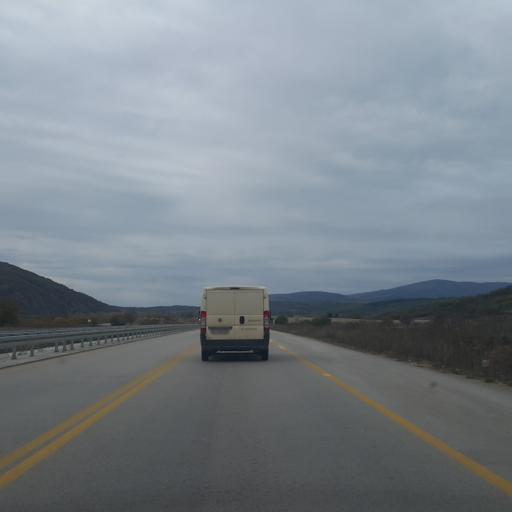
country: RS
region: Central Serbia
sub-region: Pirotski Okrug
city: Pirot
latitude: 43.2234
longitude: 22.4811
